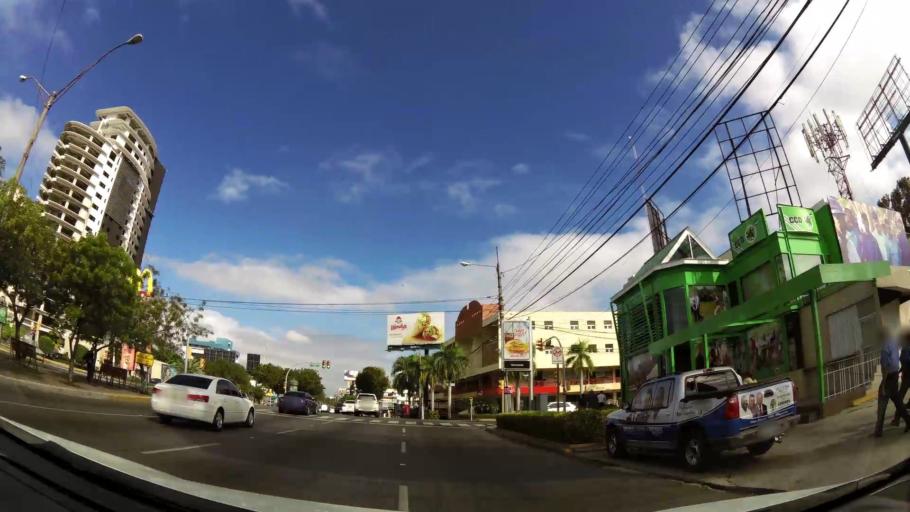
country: DO
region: Nacional
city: La Julia
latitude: 18.4584
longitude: -69.9319
